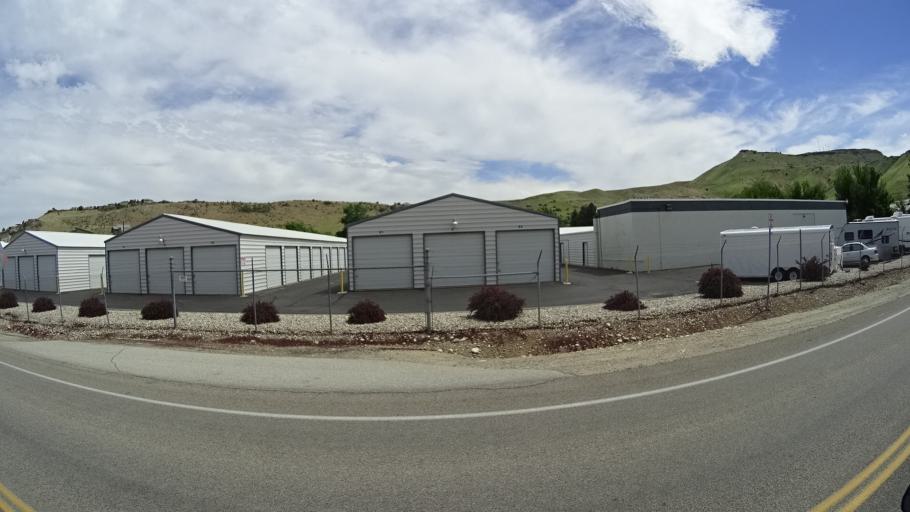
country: US
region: Idaho
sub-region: Ada County
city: Boise
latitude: 43.5992
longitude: -116.1661
